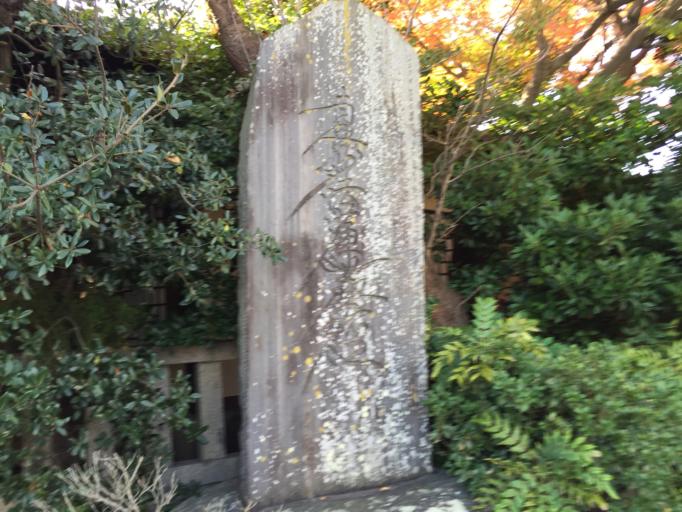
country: JP
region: Shizuoka
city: Numazu
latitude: 35.0750
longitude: 138.8644
